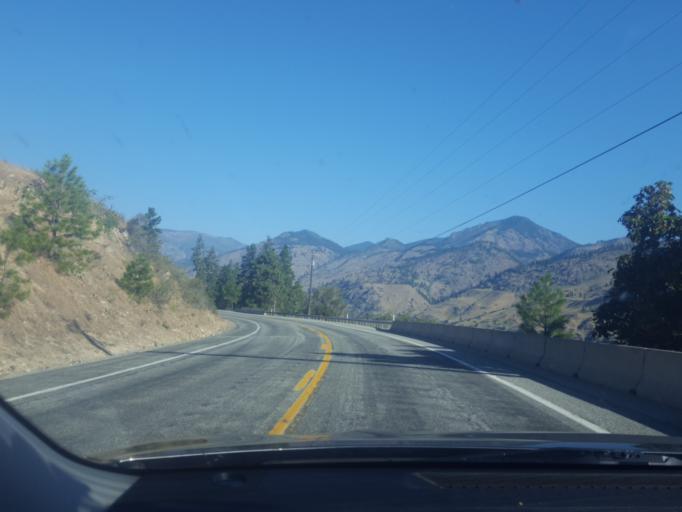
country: US
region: Washington
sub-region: Chelan County
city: Granite Falls
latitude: 47.9858
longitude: -120.2332
